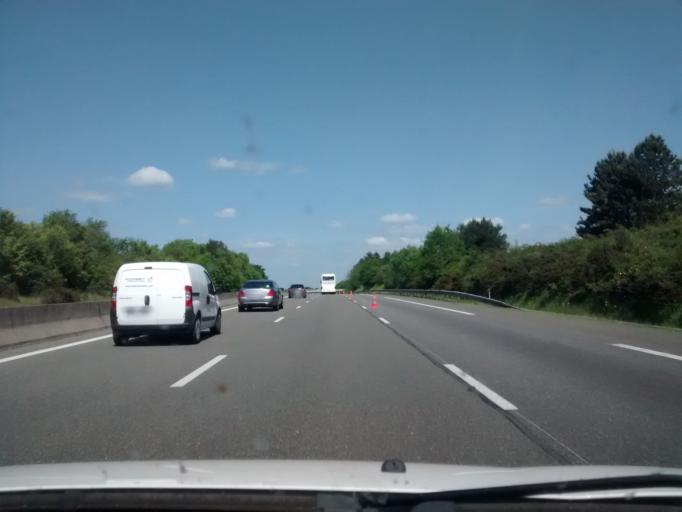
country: FR
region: Centre
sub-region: Departement d'Eure-et-Loir
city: Gallardon
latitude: 48.4912
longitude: 1.6727
